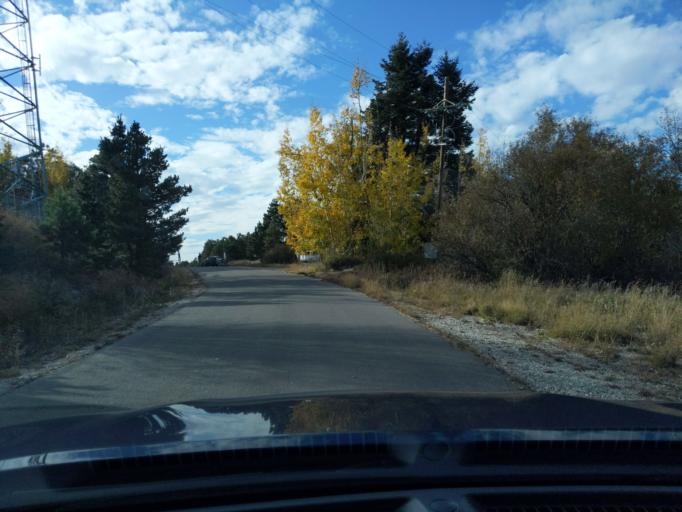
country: US
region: Arizona
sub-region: Pima County
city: Catalina
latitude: 32.4408
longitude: -110.7876
